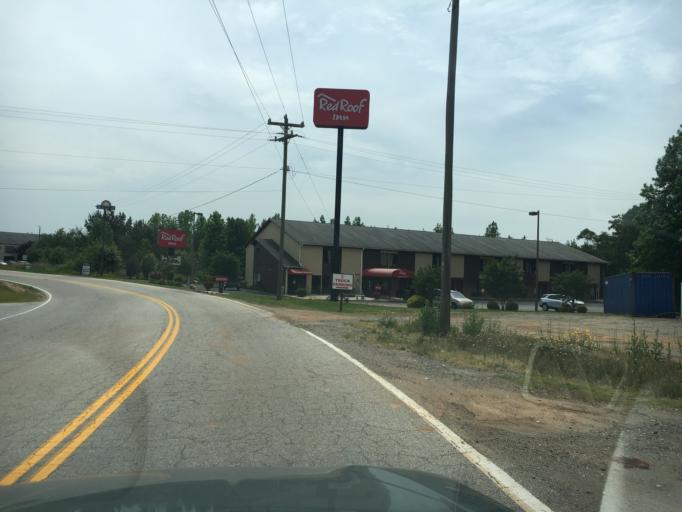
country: US
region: South Carolina
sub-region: Spartanburg County
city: Southern Shops
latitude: 34.9906
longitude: -82.0231
